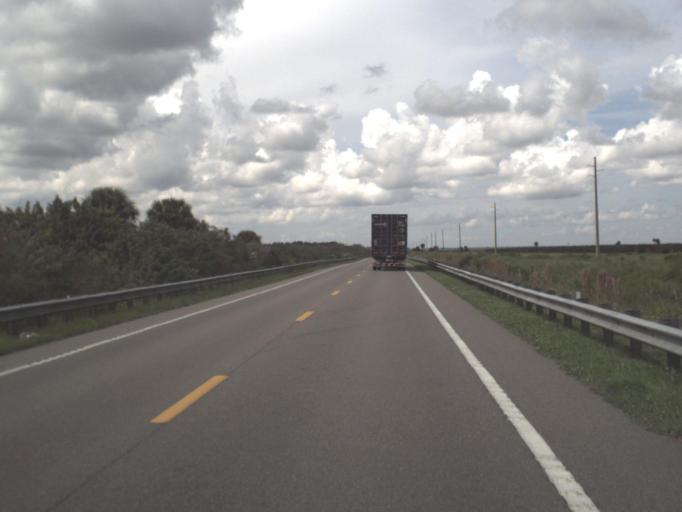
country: US
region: Florida
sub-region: Highlands County
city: Lake Placid
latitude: 27.2092
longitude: -81.1905
